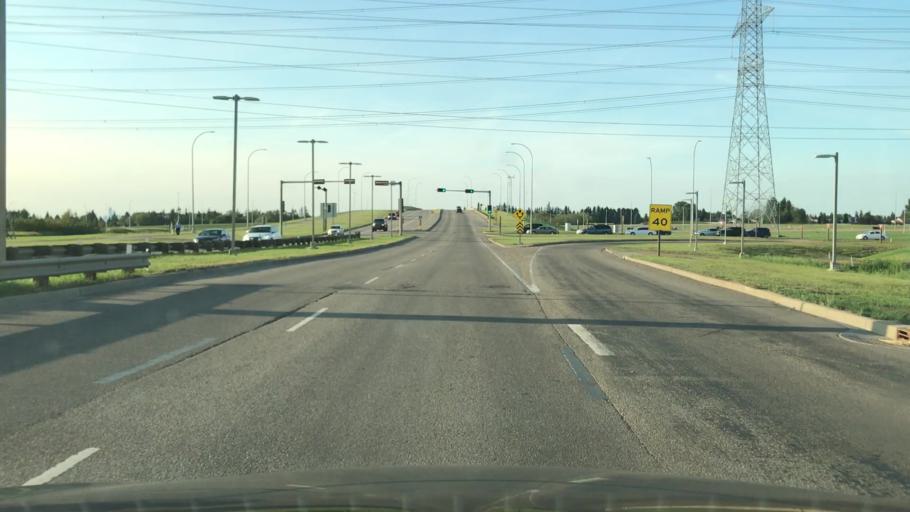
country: CA
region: Alberta
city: Beaumont
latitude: 53.4321
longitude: -113.4178
